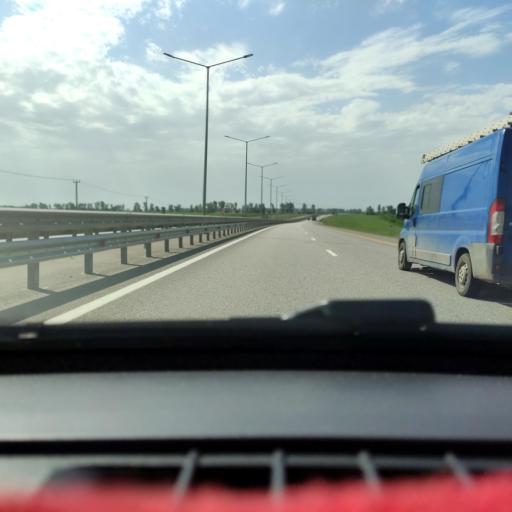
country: RU
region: Voronezj
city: Podkletnoye
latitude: 51.5316
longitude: 39.5084
